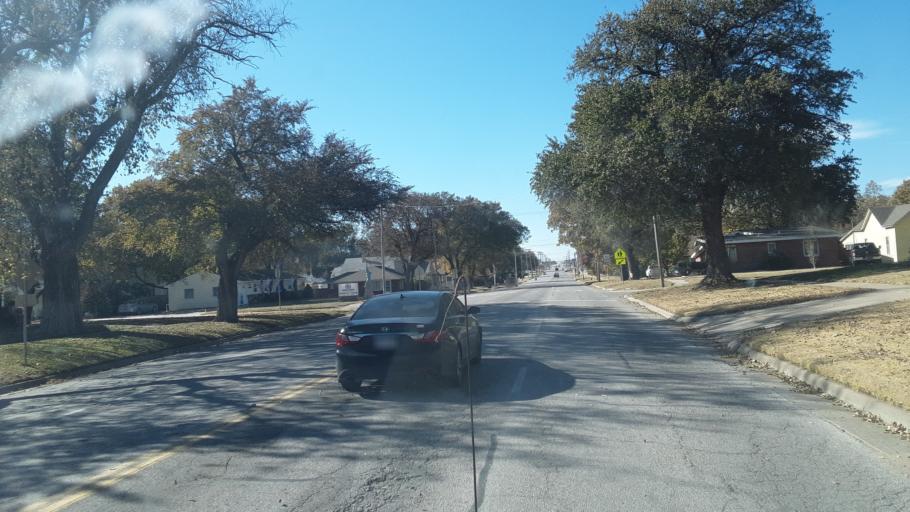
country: US
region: Kansas
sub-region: Rice County
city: Lyons
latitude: 38.3478
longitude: -98.2067
